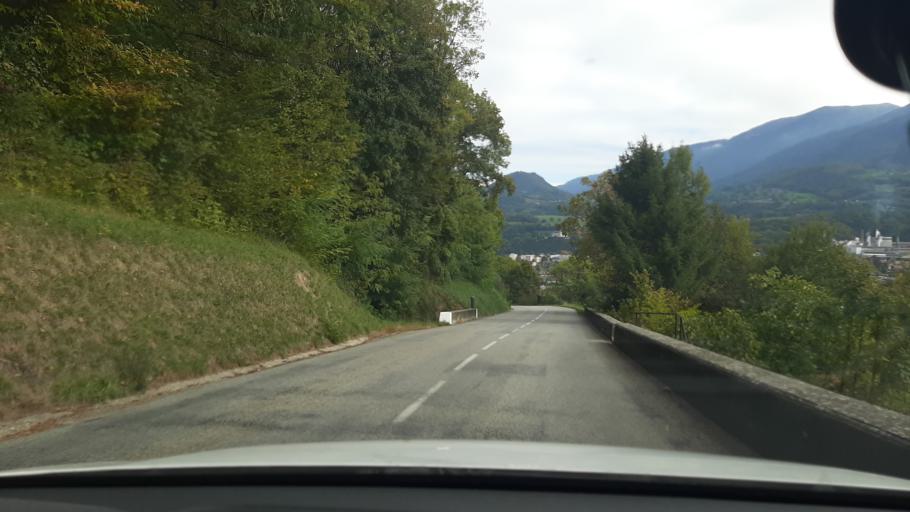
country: FR
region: Rhone-Alpes
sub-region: Departement de la Savoie
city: La Rochette
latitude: 45.4526
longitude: 6.0963
